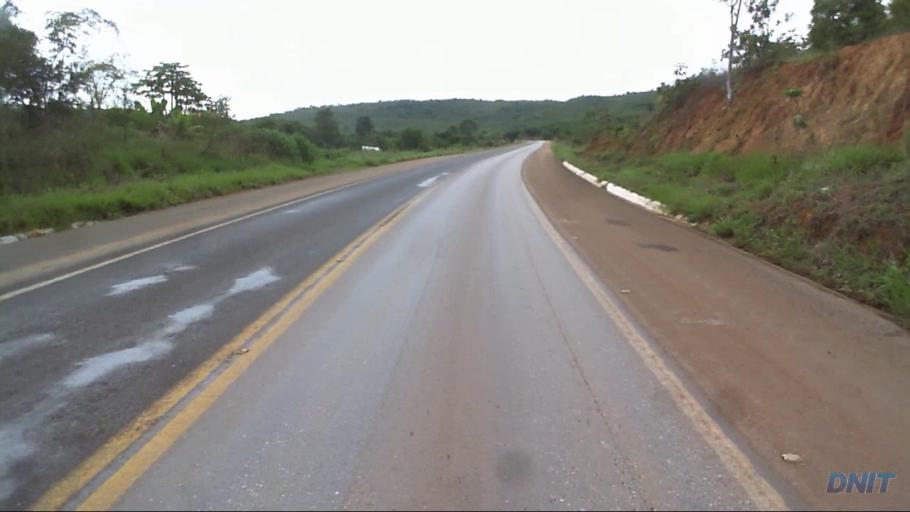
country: BR
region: Goias
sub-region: Barro Alto
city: Barro Alto
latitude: -14.9277
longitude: -48.9489
